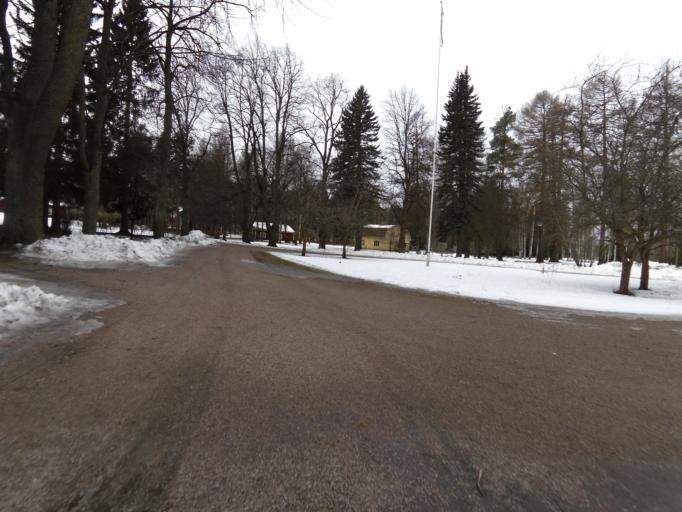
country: SE
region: Gaevleborg
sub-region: Gavle Kommun
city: Gavle
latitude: 60.6700
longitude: 17.1134
